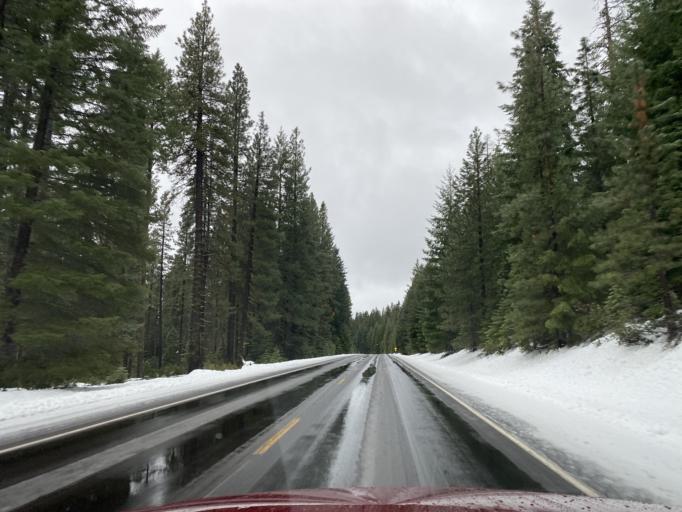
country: US
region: Oregon
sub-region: Klamath County
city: Klamath Falls
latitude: 42.4993
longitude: -122.0841
